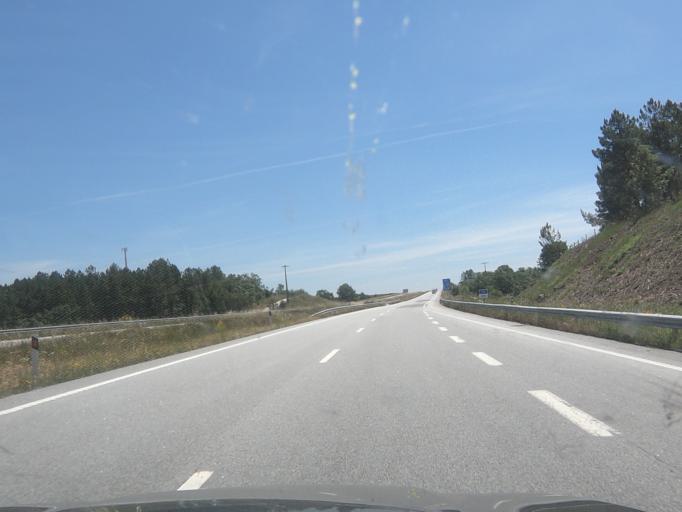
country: PT
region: Guarda
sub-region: Pinhel
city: Pinhel
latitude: 40.6105
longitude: -7.0034
